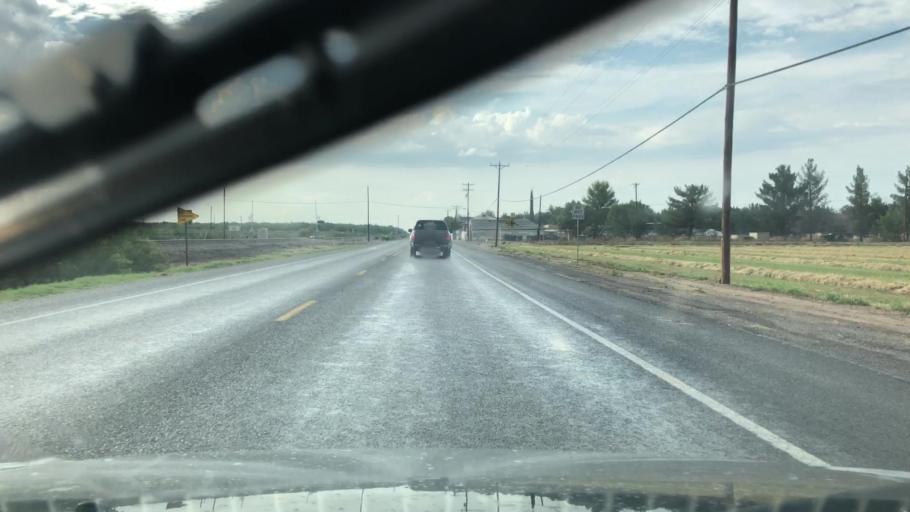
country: US
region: New Mexico
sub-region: Dona Ana County
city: Mesquite
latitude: 32.2076
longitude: -106.7237
